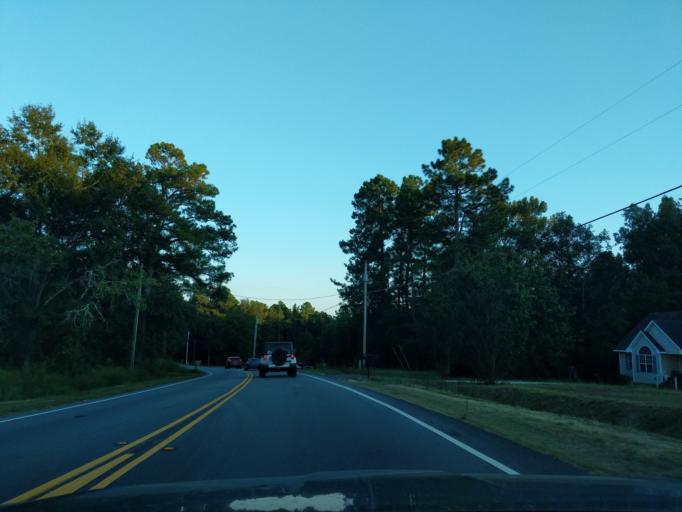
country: US
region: South Carolina
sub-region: Aiken County
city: Burnettown
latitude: 33.5316
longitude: -81.8599
